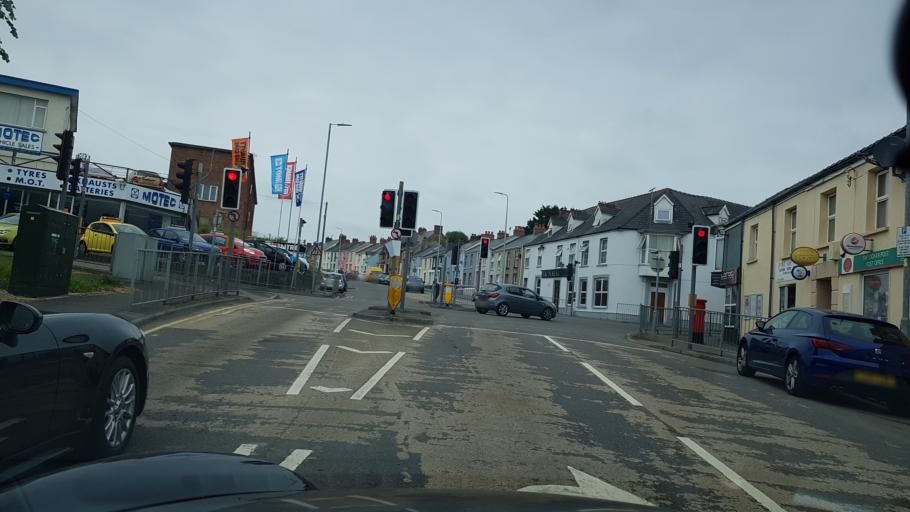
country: GB
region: Wales
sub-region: Pembrokeshire
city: Haverfordwest
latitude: 51.7983
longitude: -4.9745
